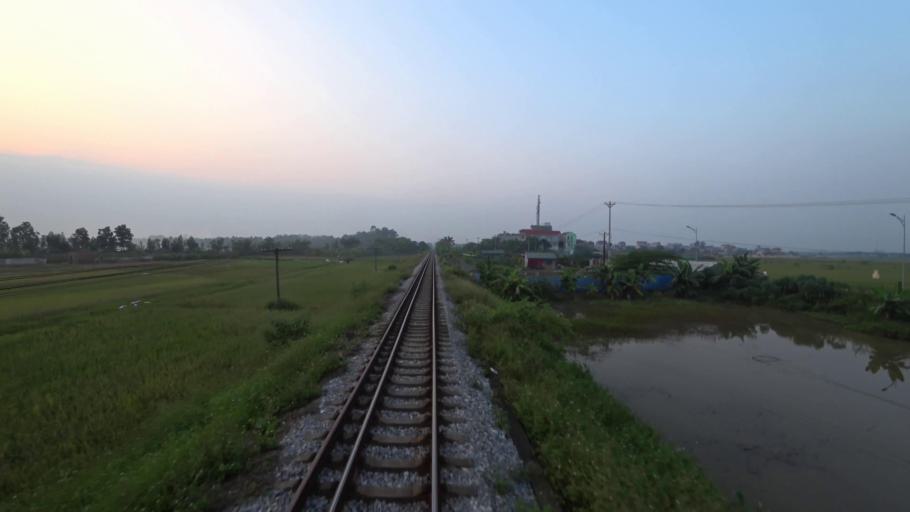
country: VN
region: Ha Noi
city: Dong Anh
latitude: 21.1307
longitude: 105.8757
